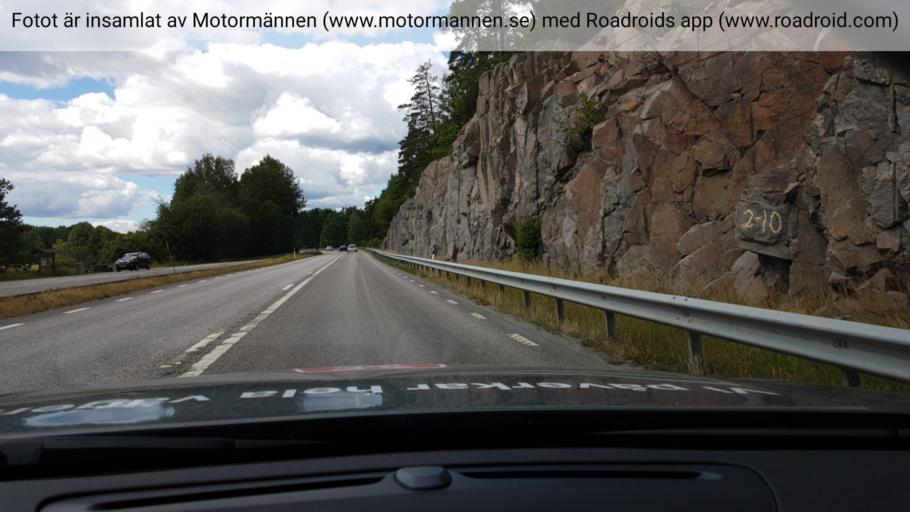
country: SE
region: Stockholm
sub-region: Osterakers Kommun
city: Akersberga
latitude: 59.4265
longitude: 18.2659
